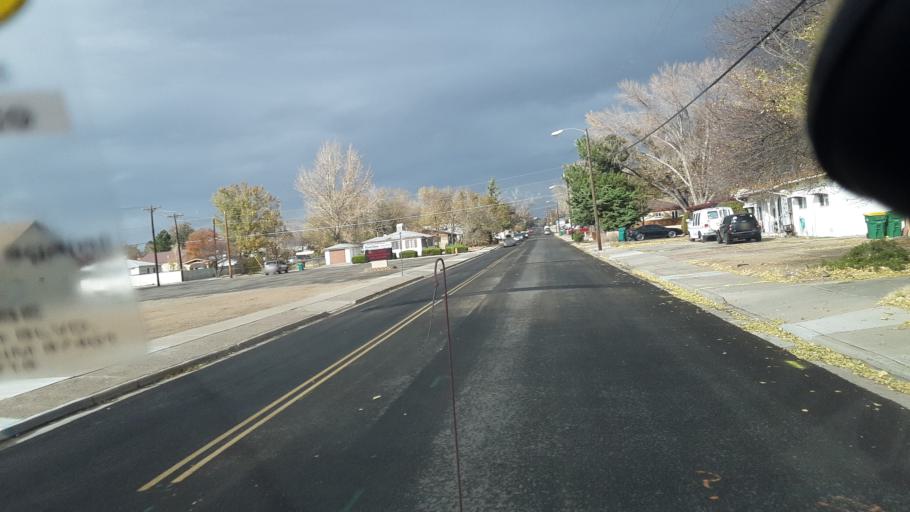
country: US
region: New Mexico
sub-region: San Juan County
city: Farmington
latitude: 36.7375
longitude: -108.1979
